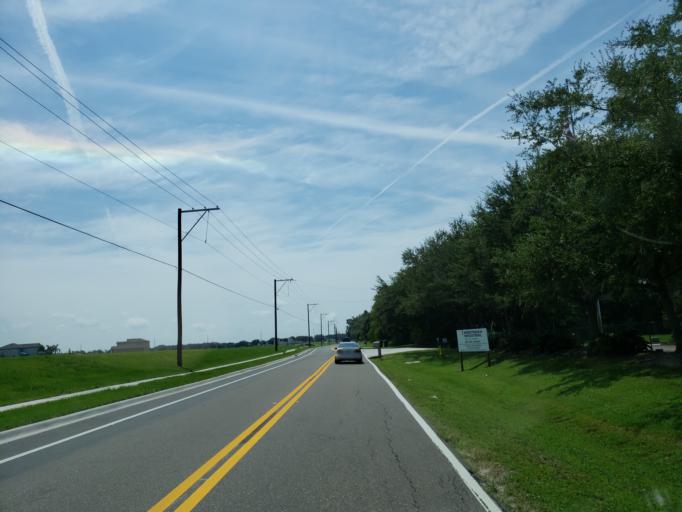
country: US
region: Florida
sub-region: Hillsborough County
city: Riverview
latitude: 27.8424
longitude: -82.3433
